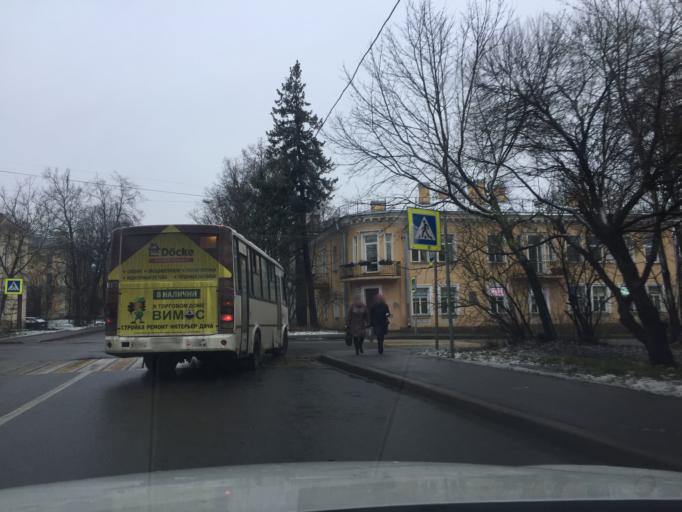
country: RU
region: St.-Petersburg
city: Pushkin
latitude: 59.7165
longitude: 30.4052
